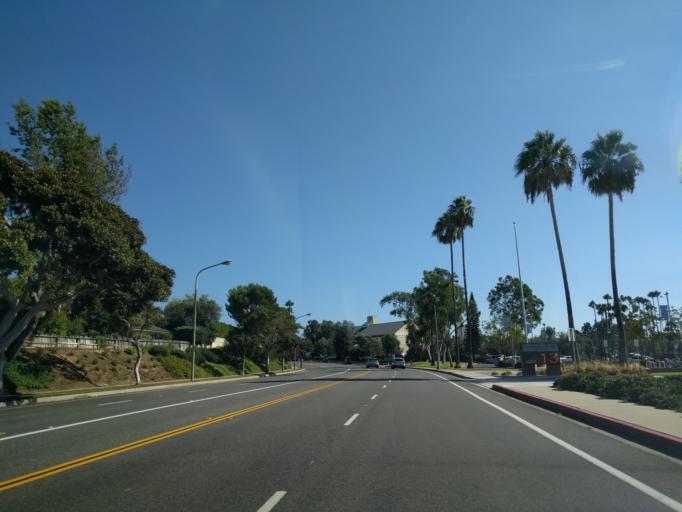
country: US
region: California
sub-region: Orange County
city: Costa Mesa
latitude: 33.6336
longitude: -117.8760
